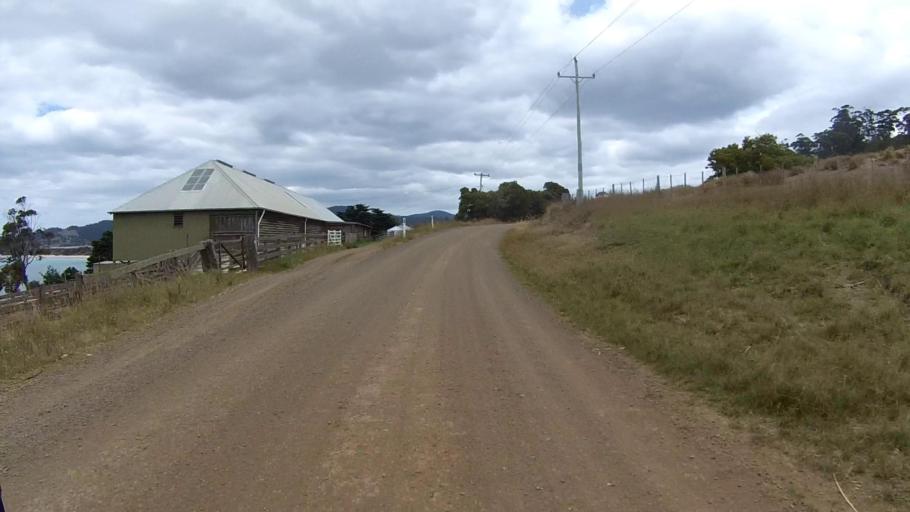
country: AU
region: Tasmania
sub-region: Sorell
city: Sorell
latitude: -42.6267
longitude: 147.9326
